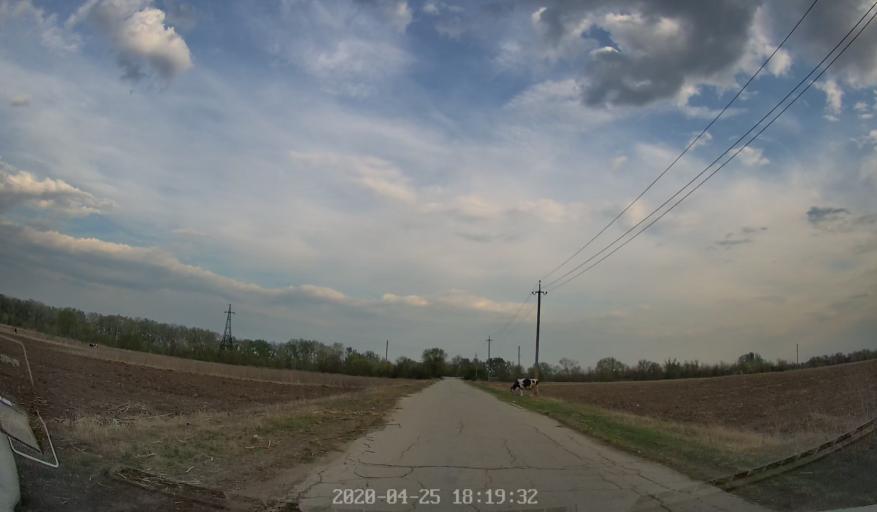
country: MD
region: Criuleni
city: Criuleni
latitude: 47.1594
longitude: 29.1310
